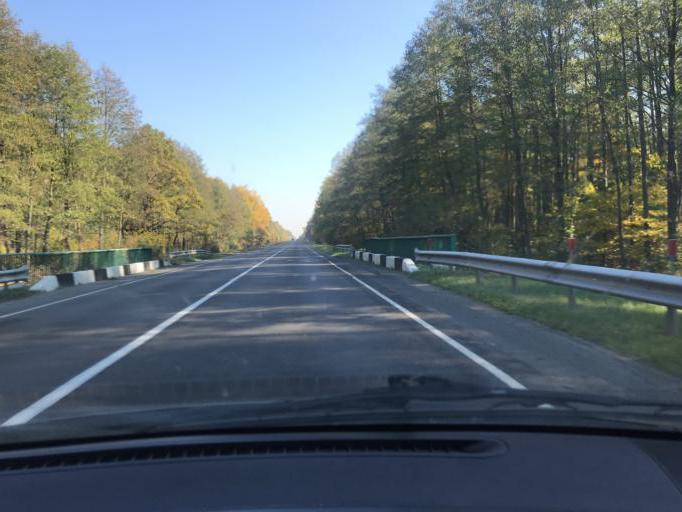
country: BY
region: Brest
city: Mikashevichy
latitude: 52.2400
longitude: 27.3000
